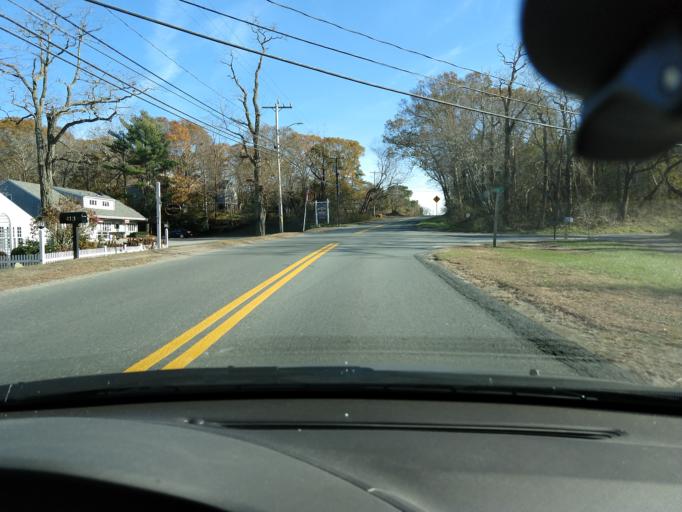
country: US
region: Massachusetts
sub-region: Barnstable County
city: East Sandwich
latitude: 41.7399
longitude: -70.4456
